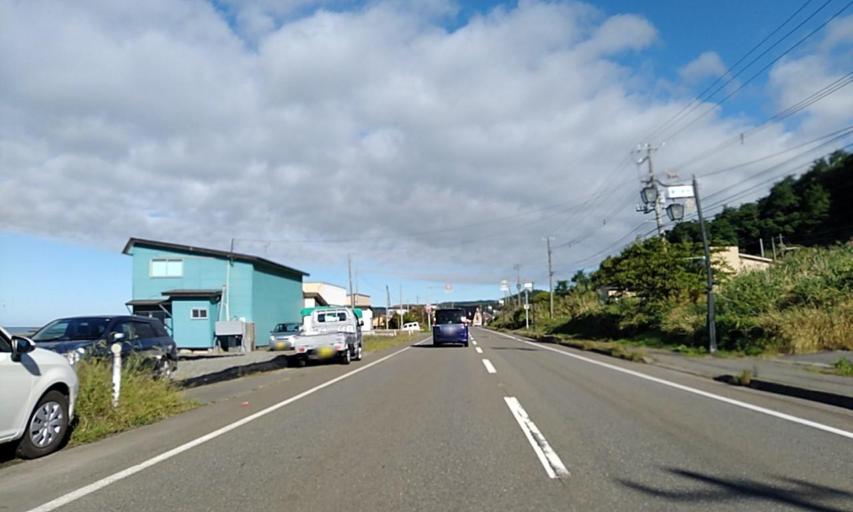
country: JP
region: Hokkaido
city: Shizunai-furukawacho
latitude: 42.2928
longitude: 142.4563
